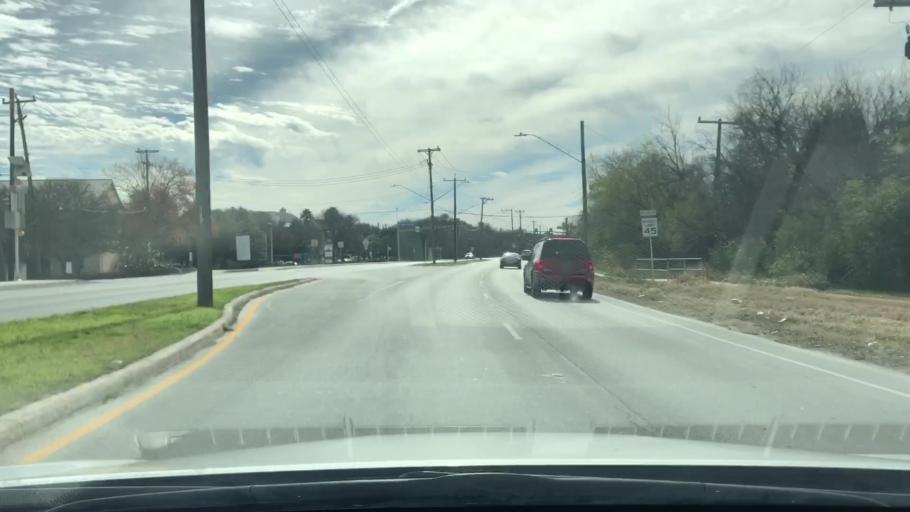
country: US
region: Texas
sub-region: Bexar County
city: Terrell Hills
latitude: 29.5107
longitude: -98.4347
